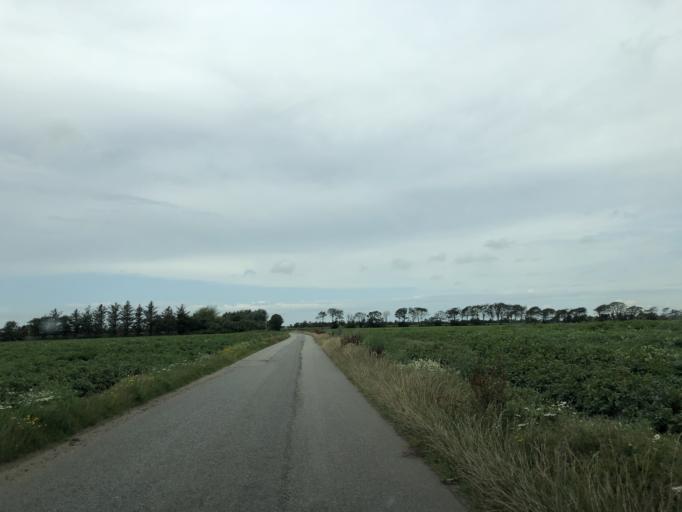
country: DK
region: Central Jutland
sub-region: Ringkobing-Skjern Kommune
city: Ringkobing
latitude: 56.1289
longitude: 8.2722
